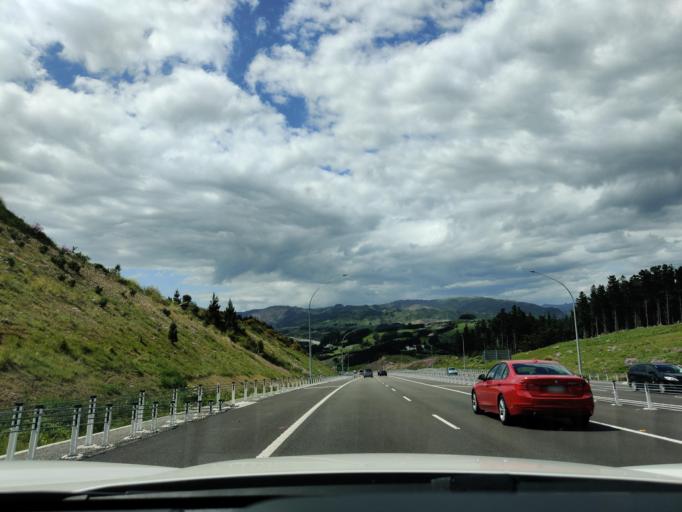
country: NZ
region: Wellington
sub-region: Porirua City
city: Porirua
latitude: -41.1209
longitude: 174.9098
